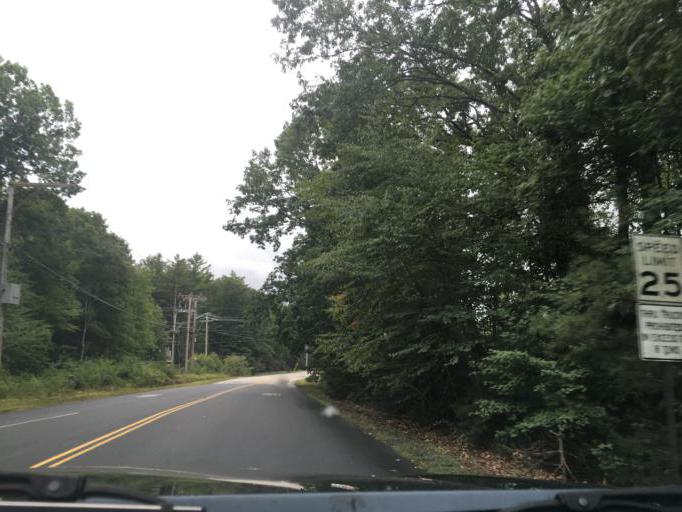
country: US
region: New Hampshire
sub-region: Rockingham County
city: Exeter
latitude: 42.9803
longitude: -70.9066
